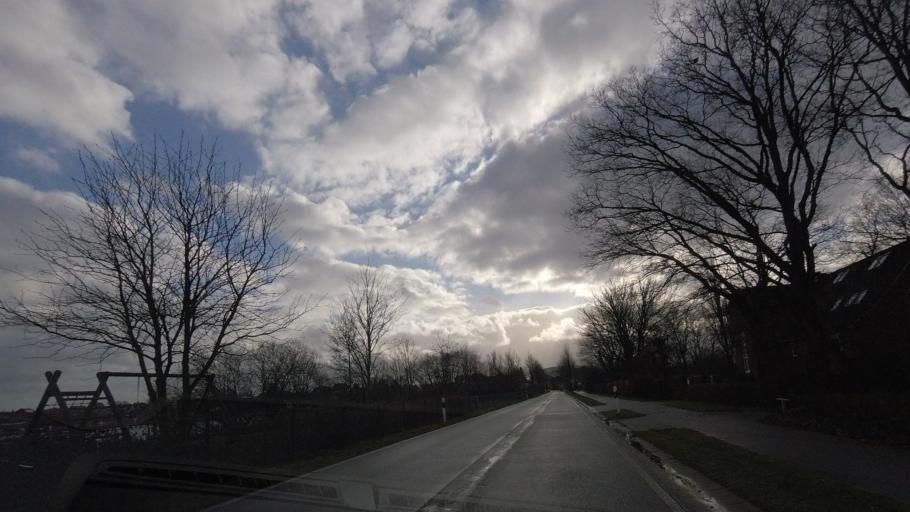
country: DE
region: Schleswig-Holstein
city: Grodersby
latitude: 54.6329
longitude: 9.9292
